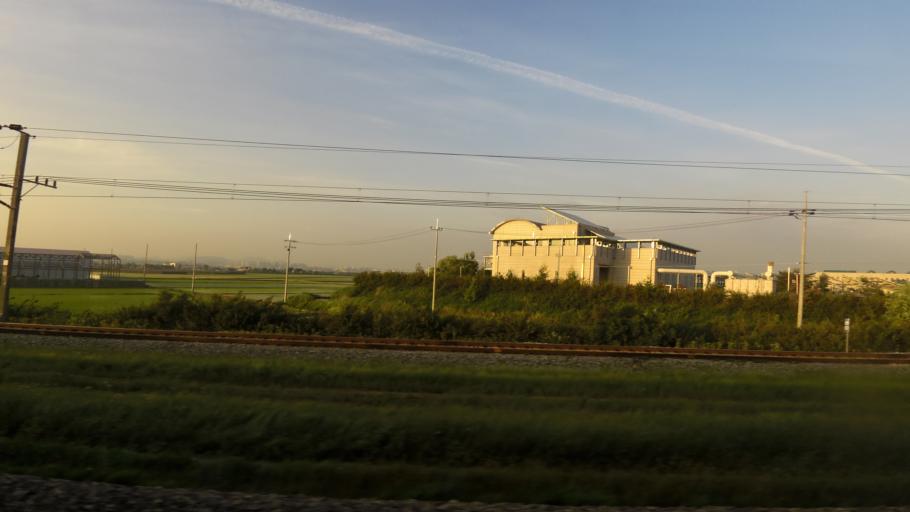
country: KR
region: Chungcheongnam-do
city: Seonghwan
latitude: 36.9577
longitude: 127.1170
